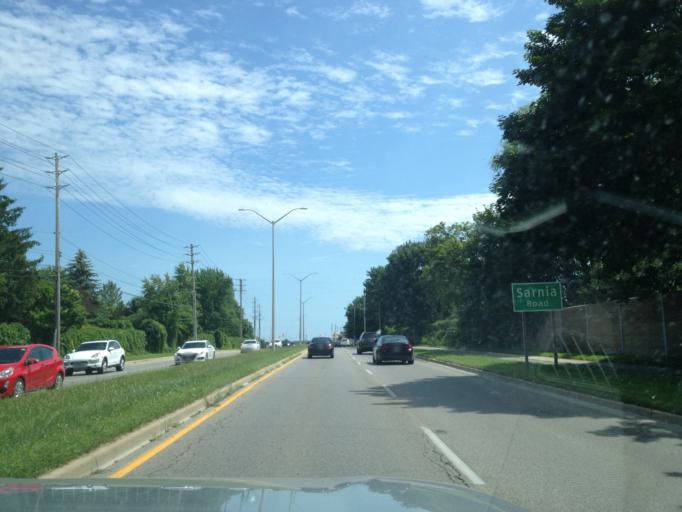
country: CA
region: Ontario
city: London
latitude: 42.9983
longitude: -81.3002
